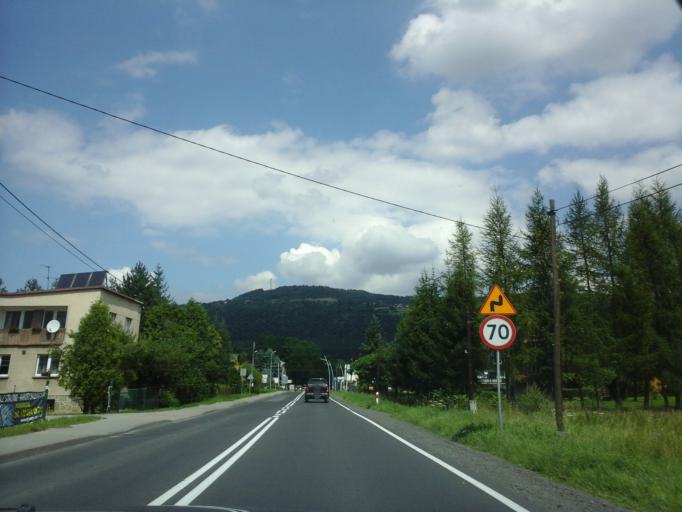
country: PL
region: Lesser Poland Voivodeship
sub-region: Powiat suski
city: Makow Podhalanski
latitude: 49.7194
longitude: 19.6878
